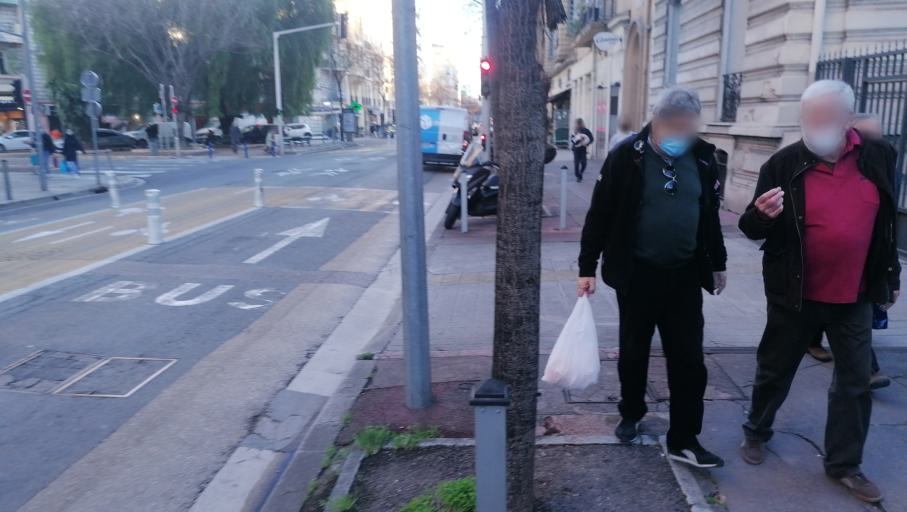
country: FR
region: Provence-Alpes-Cote d'Azur
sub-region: Departement des Alpes-Maritimes
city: Nice
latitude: 43.7012
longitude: 7.2561
